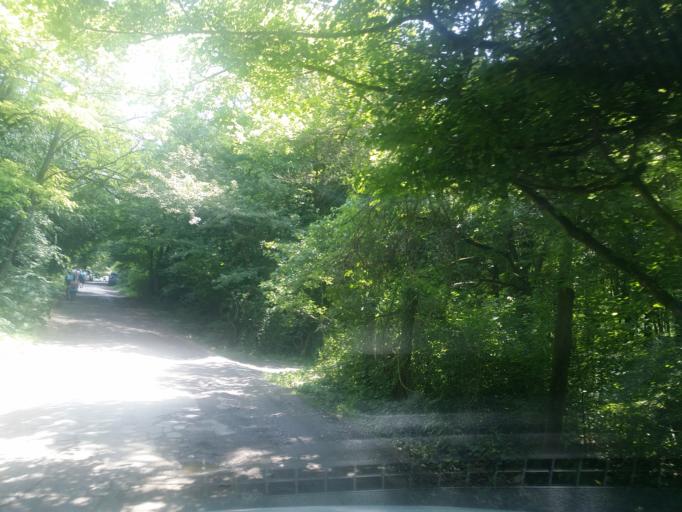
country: HU
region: Komarom-Esztergom
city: Piliscsev
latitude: 47.7035
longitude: 18.8308
